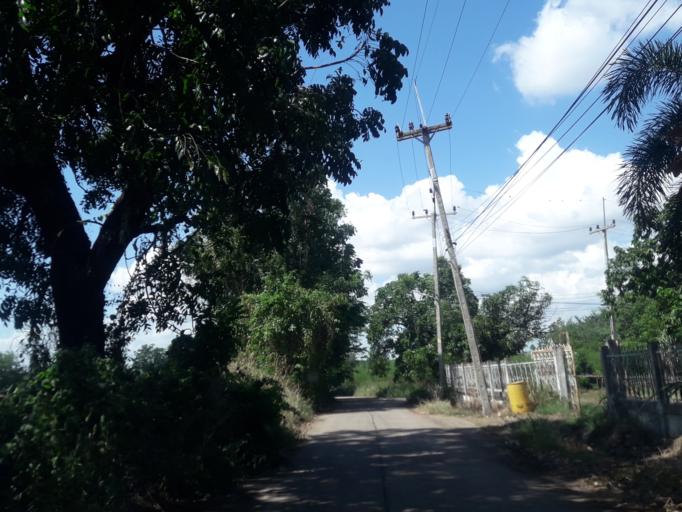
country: TH
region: Lop Buri
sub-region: Amphoe Tha Luang
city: Tha Luang
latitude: 15.0679
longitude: 101.0448
